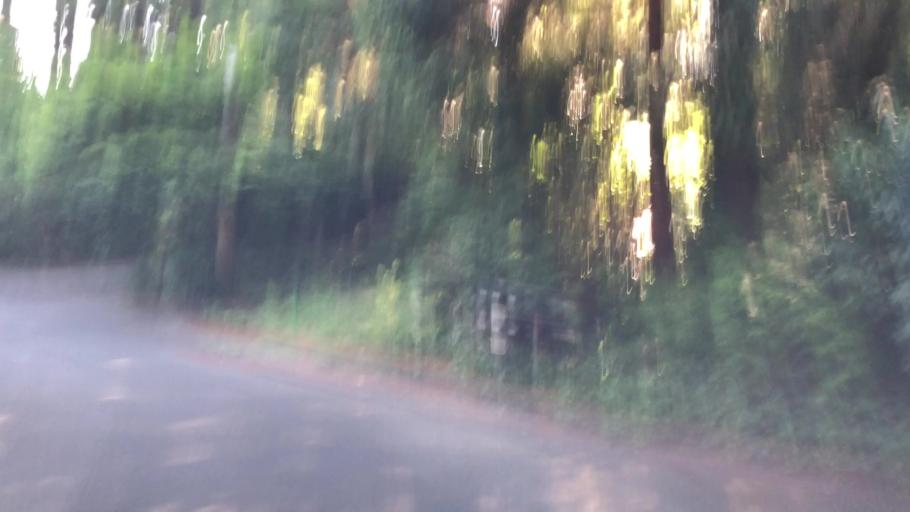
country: US
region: Washington
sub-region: King County
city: Lake Forest Park
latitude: 47.7577
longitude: -122.2734
